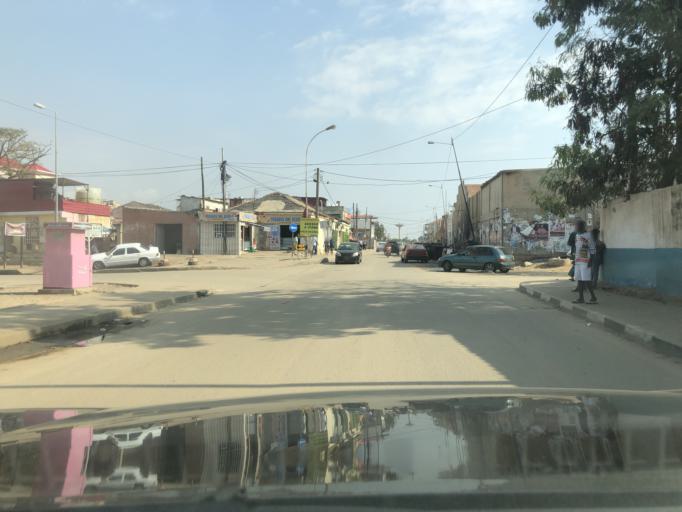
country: AO
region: Luanda
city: Luanda
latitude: -8.8479
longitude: 13.2595
